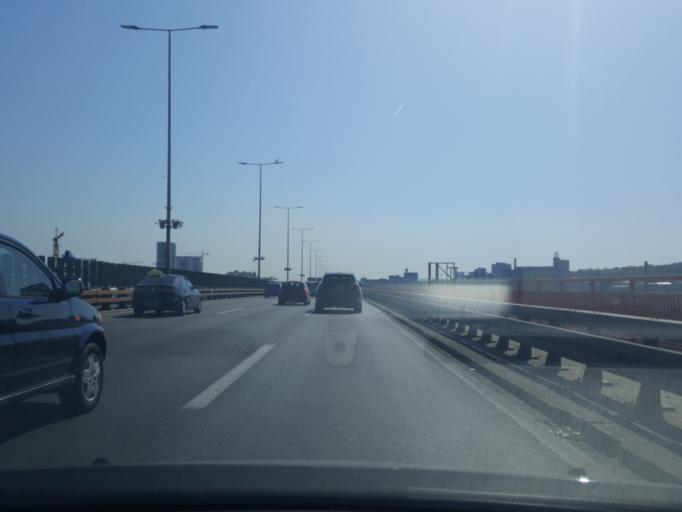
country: RS
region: Central Serbia
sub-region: Belgrade
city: Novi Beograd
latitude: 44.8029
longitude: 20.4392
